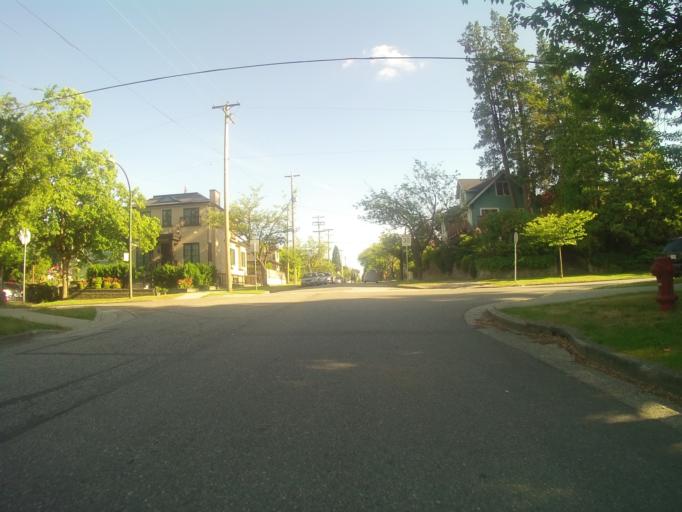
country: CA
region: British Columbia
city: Vancouver
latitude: 49.2502
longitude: -123.1204
